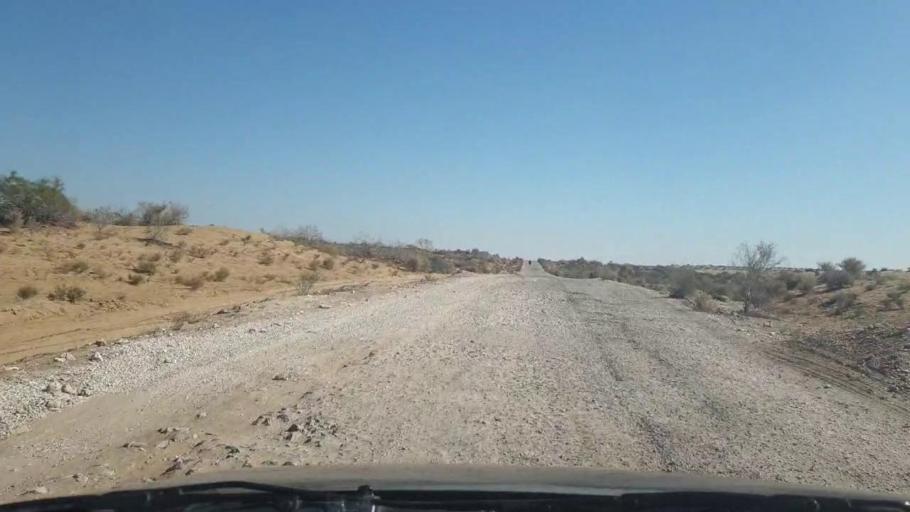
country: PK
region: Sindh
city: Bozdar
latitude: 26.9997
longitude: 68.8525
